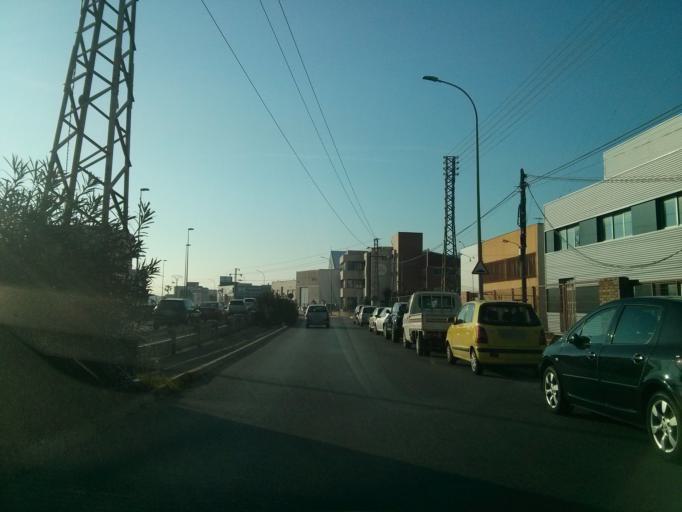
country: ES
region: Valencia
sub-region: Provincia de Valencia
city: Manises
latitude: 39.5196
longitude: -0.4622
